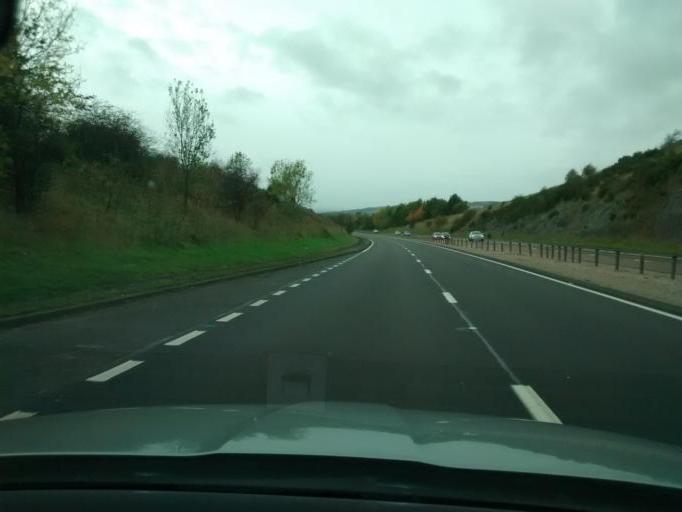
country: GB
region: Scotland
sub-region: Perth and Kinross
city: Methven
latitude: 56.3424
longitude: -3.5975
